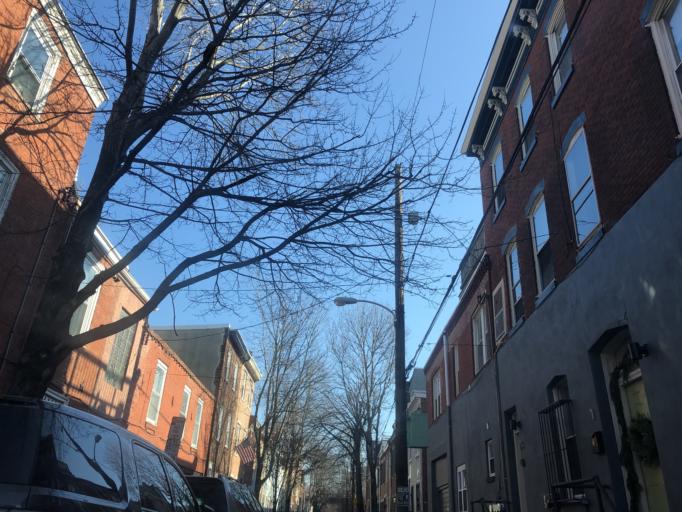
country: US
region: Pennsylvania
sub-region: Philadelphia County
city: Philadelphia
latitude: 39.9433
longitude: -75.1739
